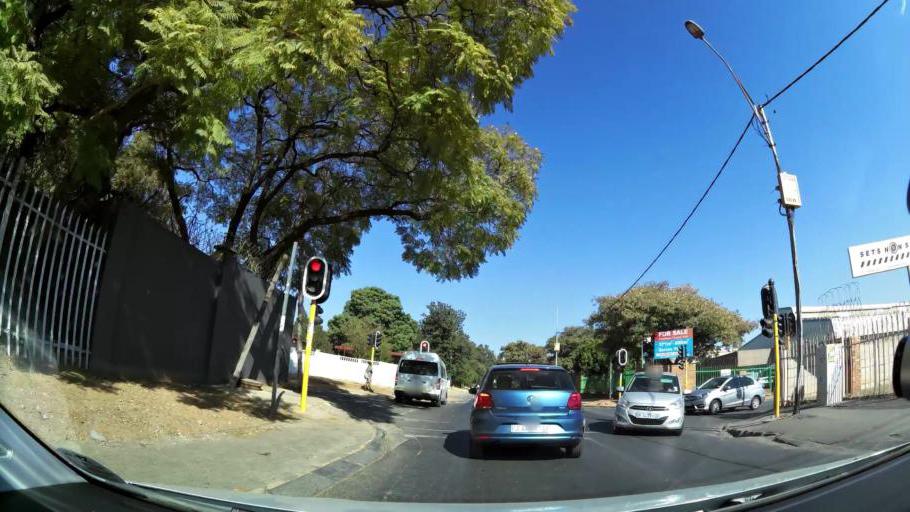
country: ZA
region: Gauteng
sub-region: City of Johannesburg Metropolitan Municipality
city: Modderfontein
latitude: -26.1167
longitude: 28.0994
